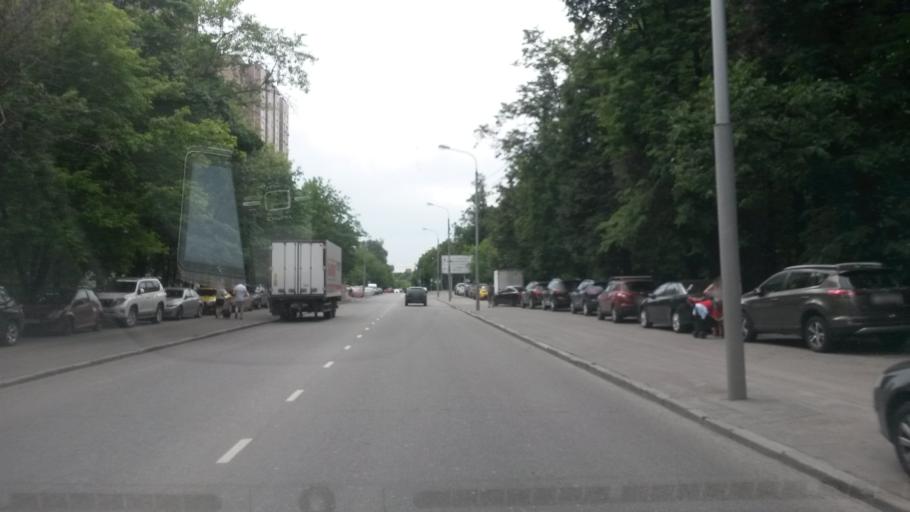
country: RU
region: Moscow
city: Sokol'niki
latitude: 55.7918
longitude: 37.6633
